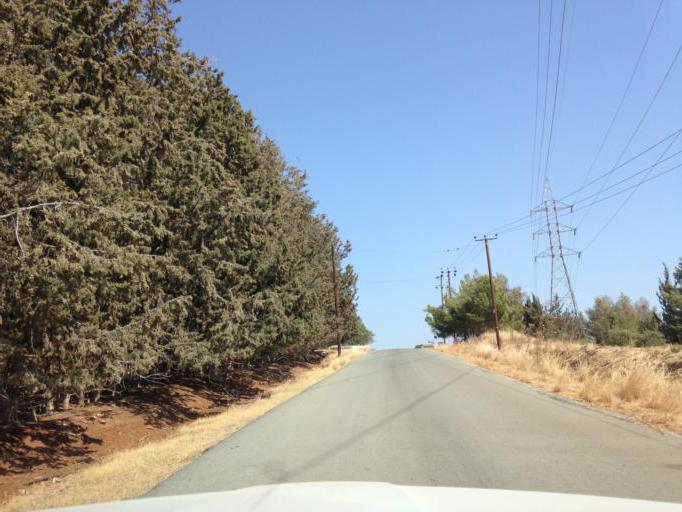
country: CY
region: Pafos
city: Mesogi
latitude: 34.7264
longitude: 32.5501
